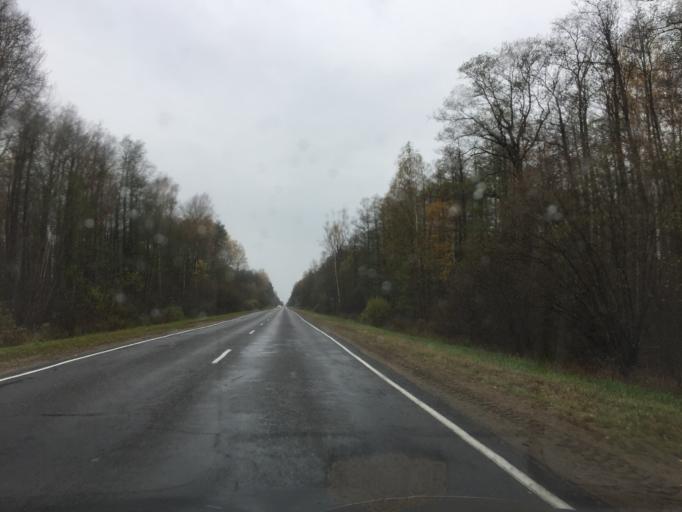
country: BY
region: Mogilev
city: Slawharad
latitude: 53.3630
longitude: 30.8467
